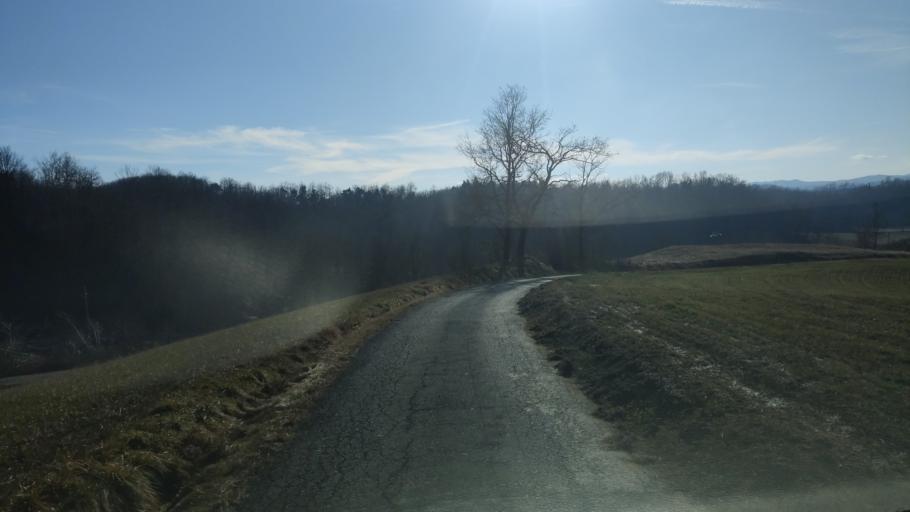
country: IT
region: Piedmont
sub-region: Provincia di Cuneo
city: Camerana
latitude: 44.4104
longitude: 8.1305
